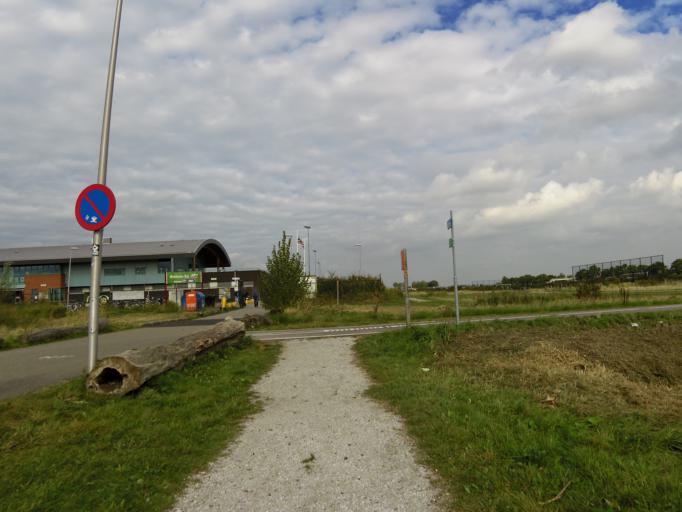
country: NL
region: South Holland
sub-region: Gemeente Rijnwoude
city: Benthuizen
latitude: 52.0649
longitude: 4.5556
